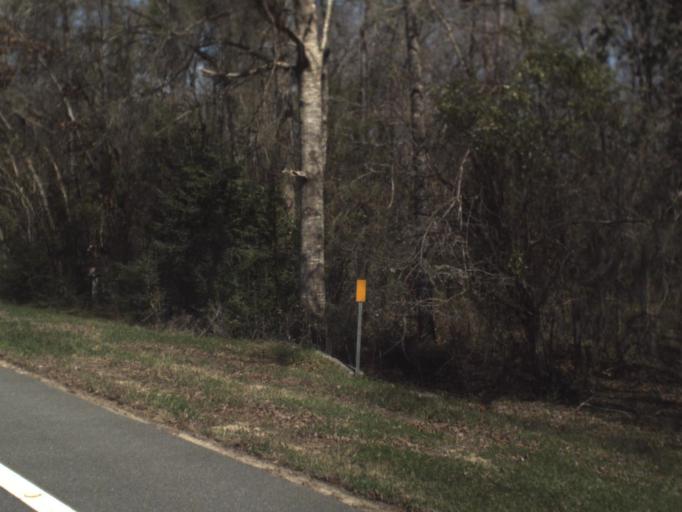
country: US
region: Florida
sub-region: Jackson County
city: Sneads
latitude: 30.6475
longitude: -85.0384
